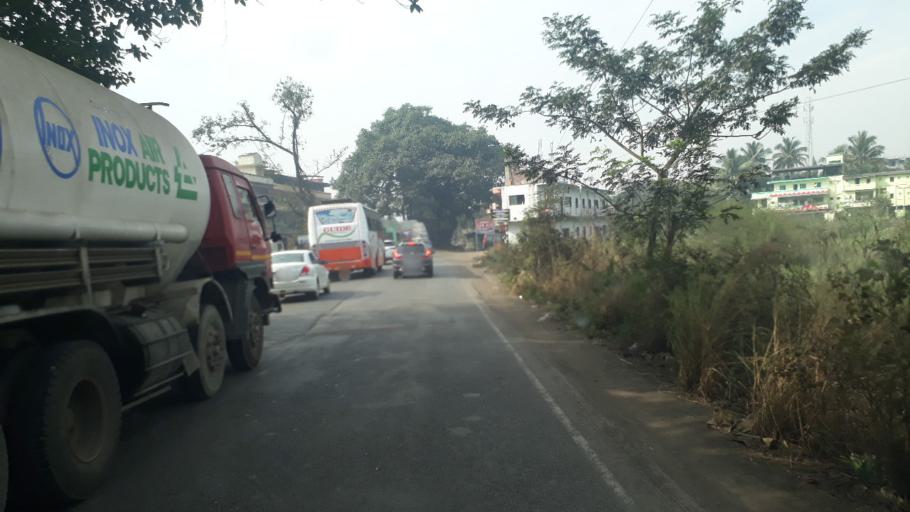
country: IN
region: Maharashtra
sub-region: Raigarh
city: Pen
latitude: 18.7143
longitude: 73.0568
